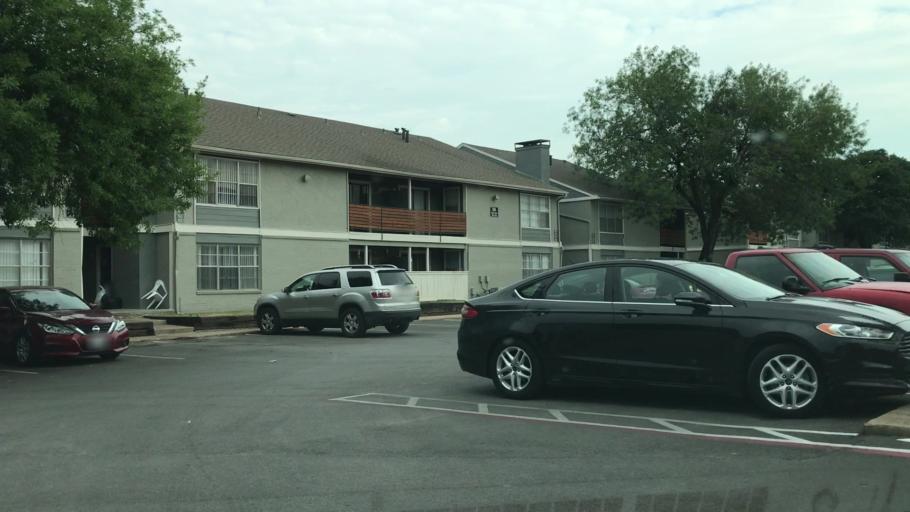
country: US
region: Texas
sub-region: Tarrant County
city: Hurst
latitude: 32.8248
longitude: -97.1663
